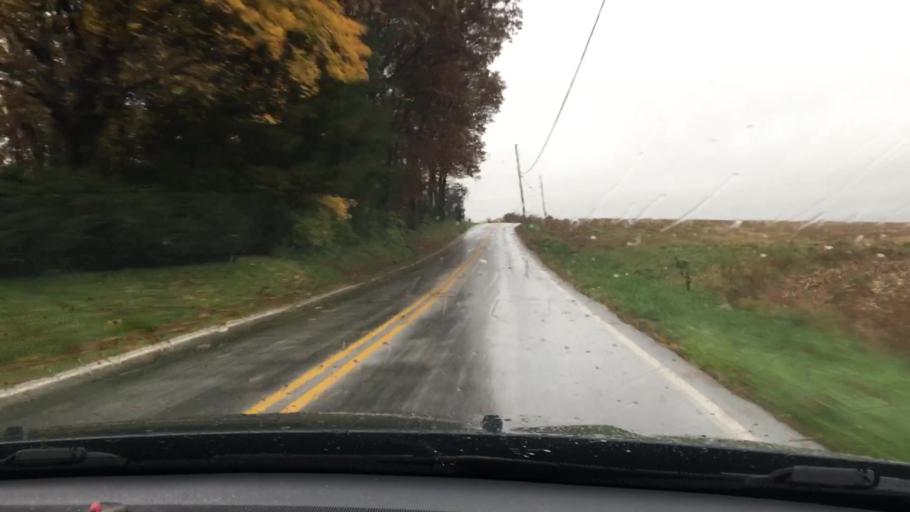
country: US
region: Pennsylvania
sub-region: York County
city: Susquehanna Trails
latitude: 39.7815
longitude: -76.4394
